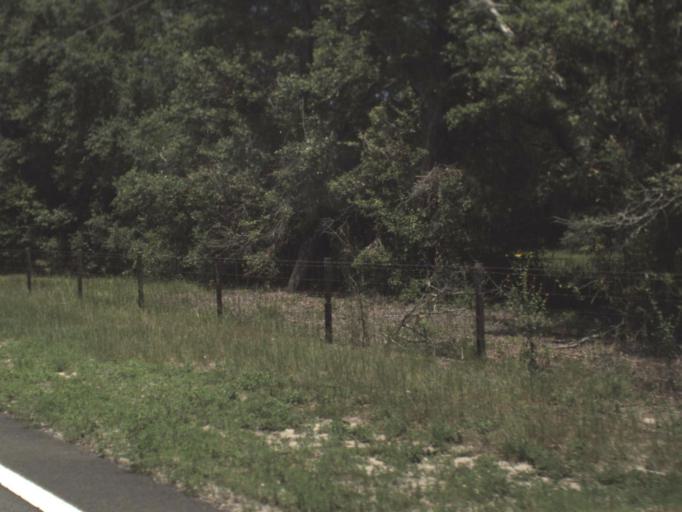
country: US
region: Florida
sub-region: Clay County
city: Keystone Heights
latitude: 29.7260
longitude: -81.9863
